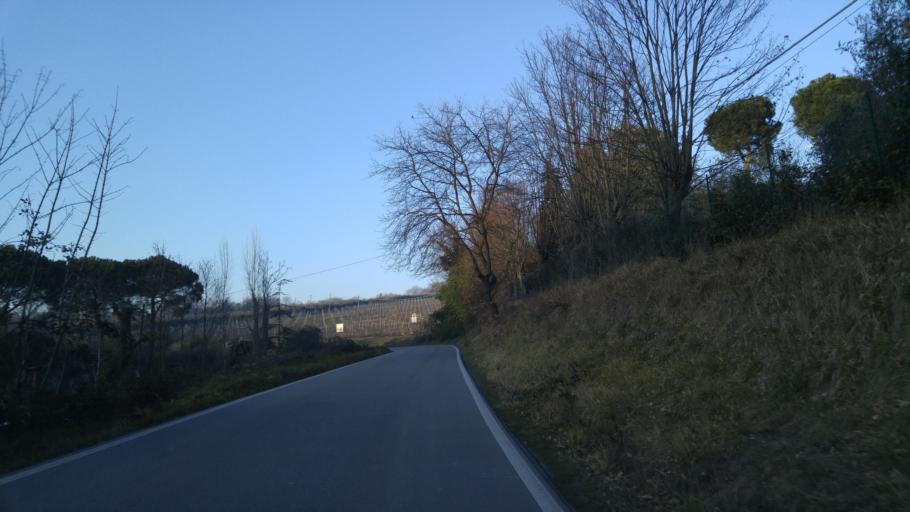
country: IT
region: The Marches
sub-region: Provincia di Pesaro e Urbino
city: Fenile
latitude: 43.8548
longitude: 12.9658
